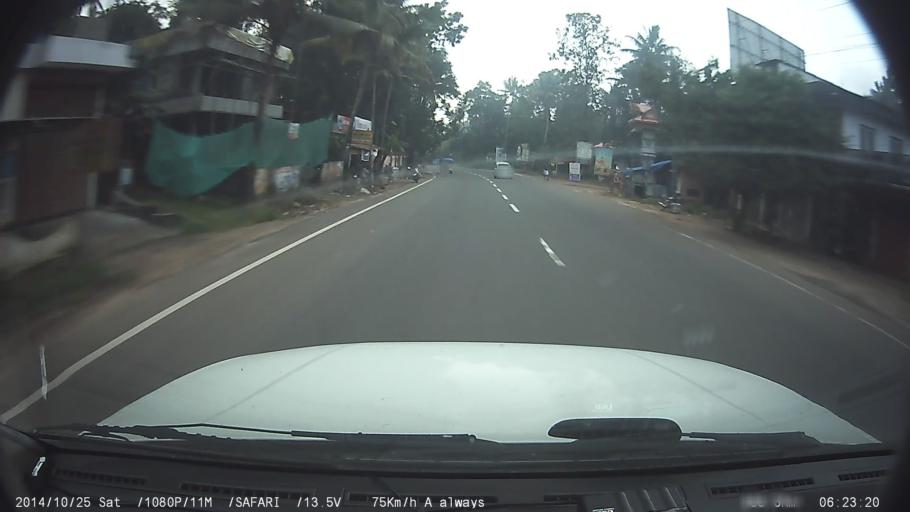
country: IN
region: Kerala
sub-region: Ernakulam
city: Perumbavoor
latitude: 10.0799
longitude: 76.5040
